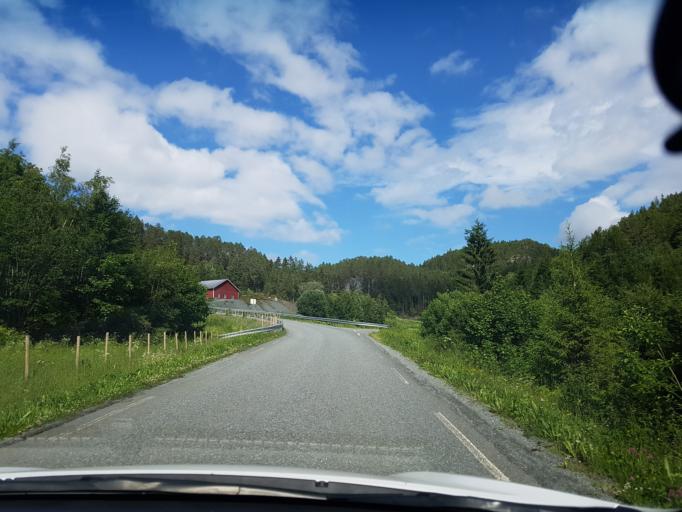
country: NO
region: Nord-Trondelag
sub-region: Frosta
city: Frosta
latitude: 63.6046
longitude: 10.8446
